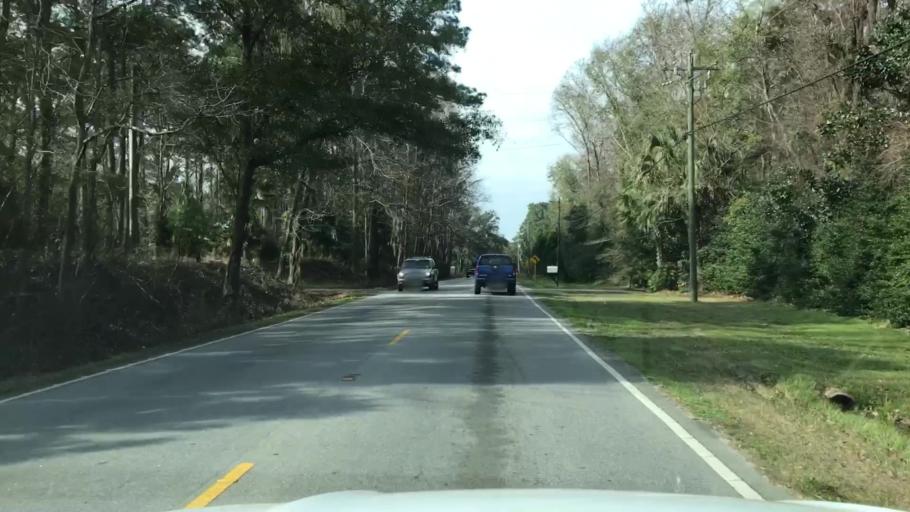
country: US
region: South Carolina
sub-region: Charleston County
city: Shell Point
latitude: 32.7789
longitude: -80.1014
